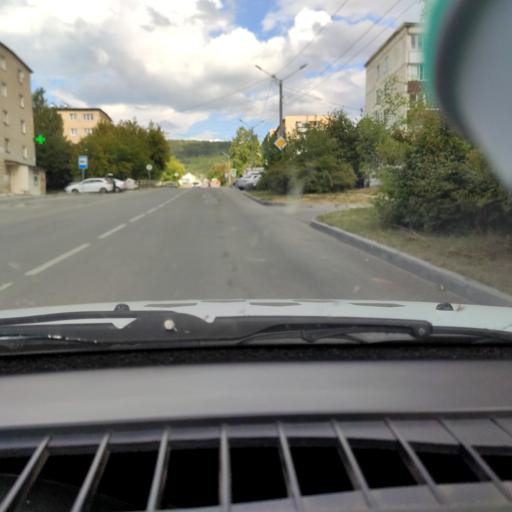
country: RU
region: Chelyabinsk
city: Miass
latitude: 55.0633
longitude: 60.1171
